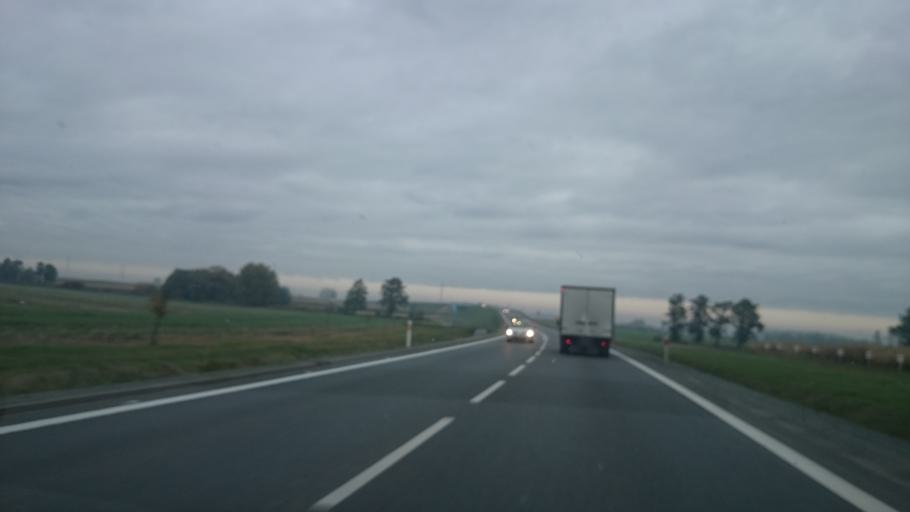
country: PL
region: Lower Silesian Voivodeship
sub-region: Powiat wroclawski
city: Kobierzyce
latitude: 50.9964
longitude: 16.9493
